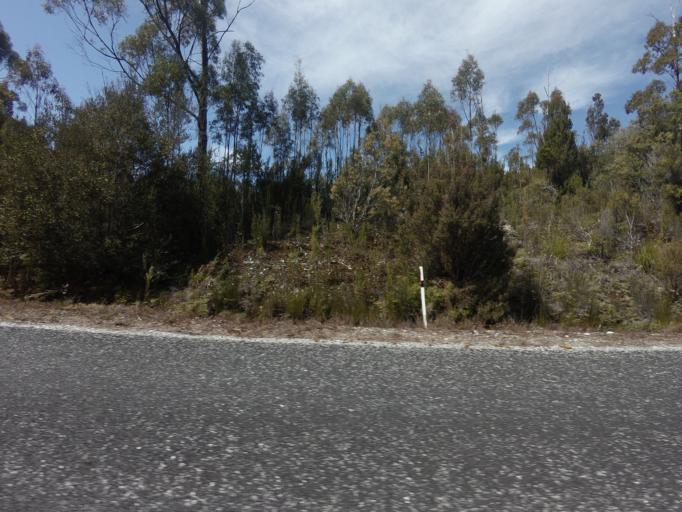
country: AU
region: Tasmania
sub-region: West Coast
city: Queenstown
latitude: -42.8032
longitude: 146.0959
